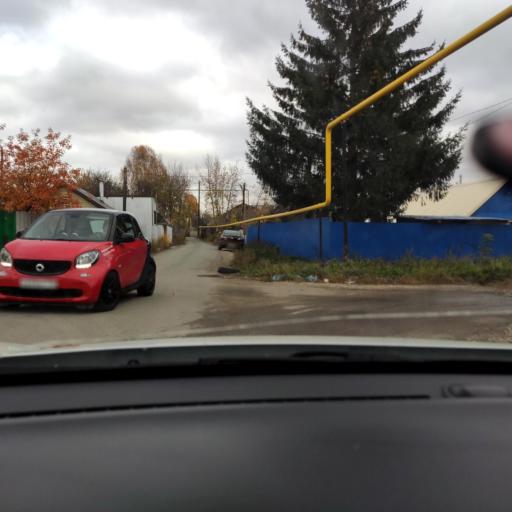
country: RU
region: Tatarstan
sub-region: Gorod Kazan'
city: Kazan
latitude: 55.7521
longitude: 49.1111
